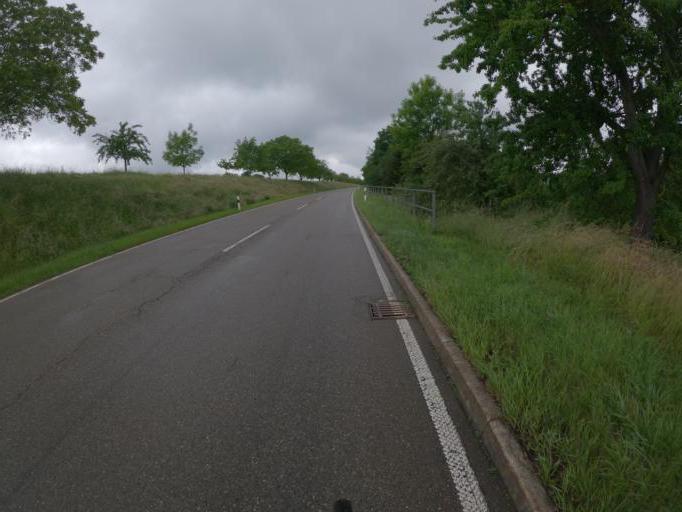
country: DE
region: Baden-Wuerttemberg
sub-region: Regierungsbezirk Stuttgart
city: Adelberg
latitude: 48.7552
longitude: 9.6048
